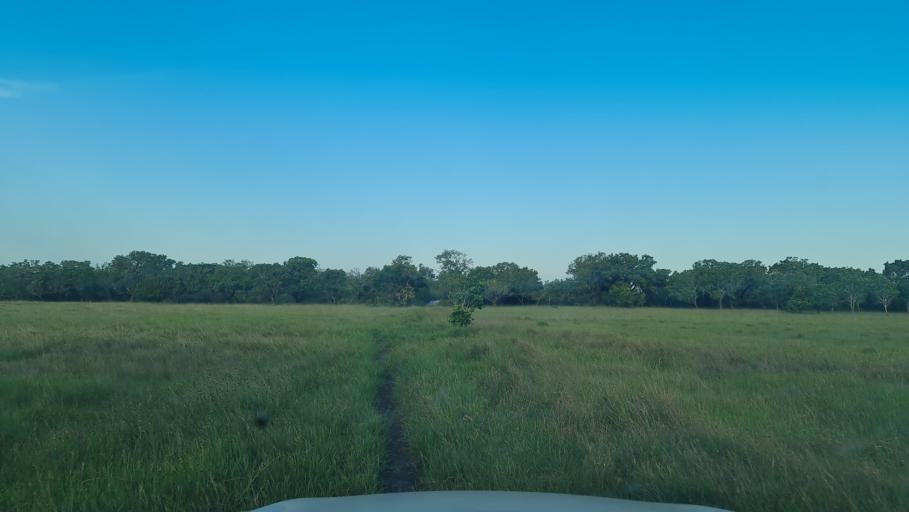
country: MZ
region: Gaza
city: Macia
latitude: -25.2215
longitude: 33.0310
